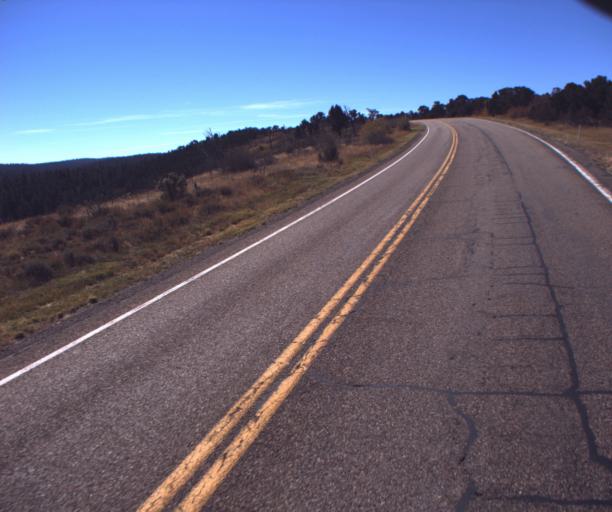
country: US
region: Arizona
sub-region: Coconino County
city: Fredonia
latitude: 36.8102
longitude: -112.2554
